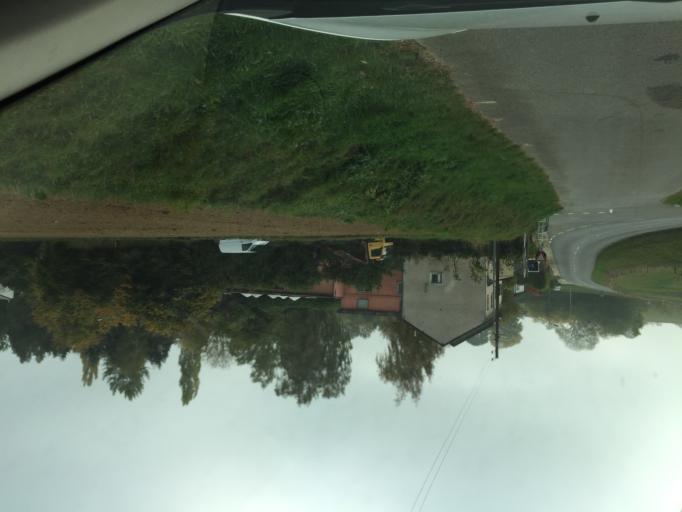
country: LU
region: Luxembourg
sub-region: Canton de Luxembourg
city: Sandweiler
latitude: 49.6214
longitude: 6.2109
